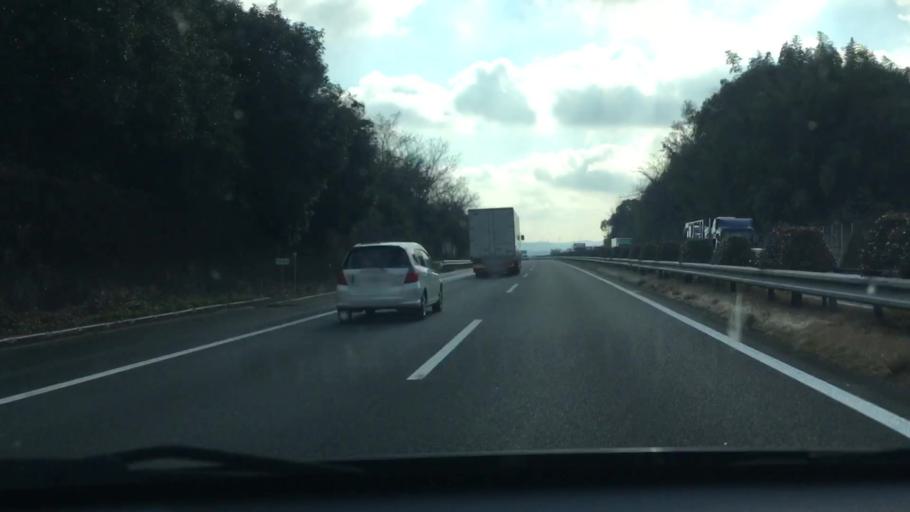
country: JP
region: Kumamoto
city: Uto
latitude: 32.7254
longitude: 130.7722
